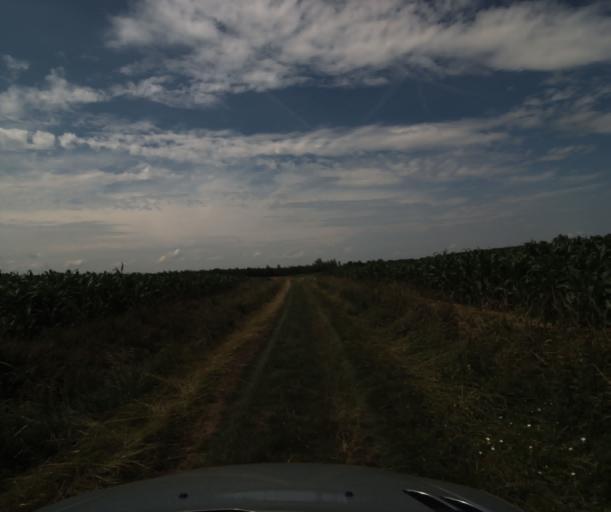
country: FR
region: Midi-Pyrenees
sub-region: Departement de la Haute-Garonne
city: Labastidette
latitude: 43.4827
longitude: 1.2222
